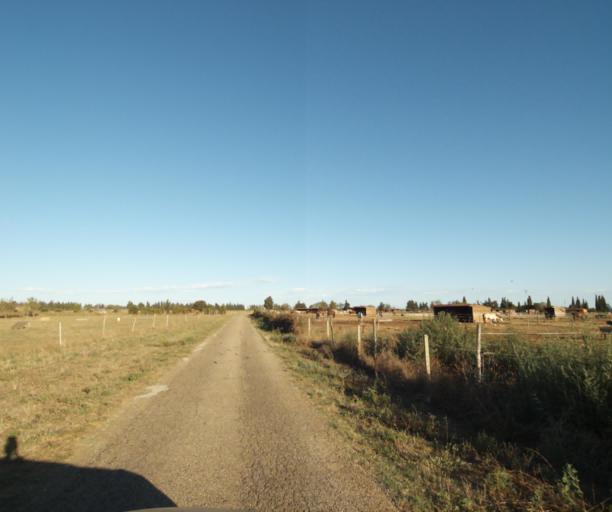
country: FR
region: Languedoc-Roussillon
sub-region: Departement du Gard
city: Garons
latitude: 43.7808
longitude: 4.4583
